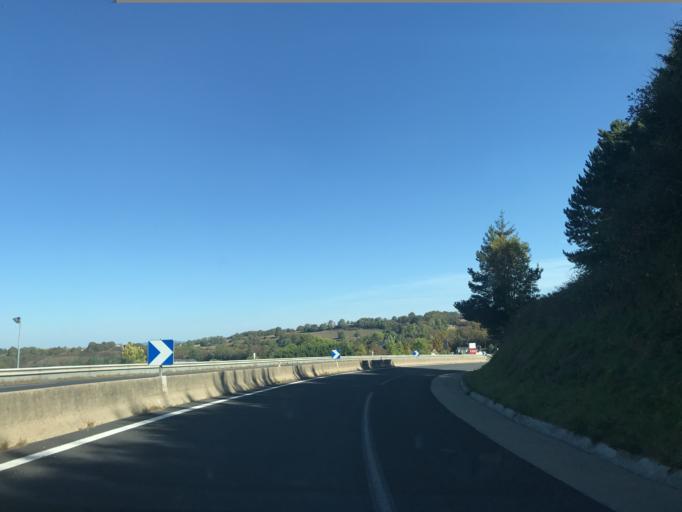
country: FR
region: Auvergne
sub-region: Departement du Puy-de-Dome
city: Gelles
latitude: 45.6847
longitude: 2.7974
